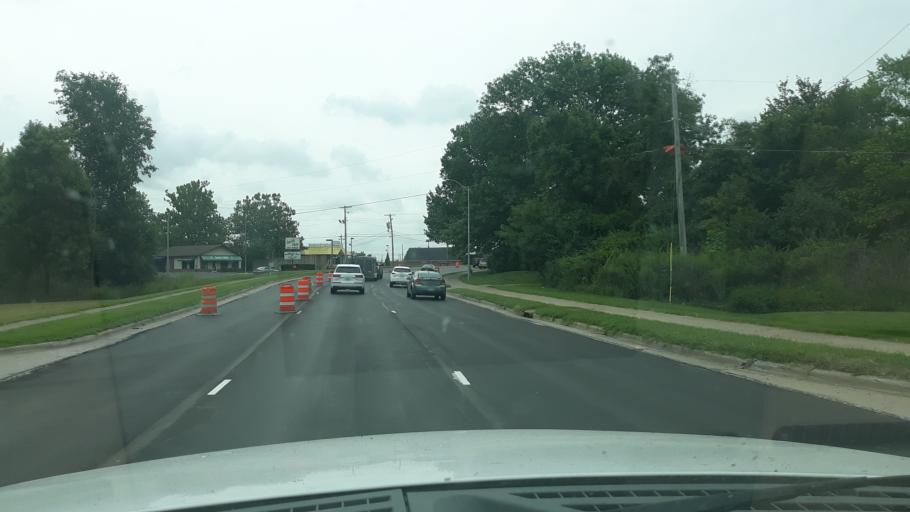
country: US
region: Illinois
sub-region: Jackson County
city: Carbondale
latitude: 37.7262
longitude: -89.2049
